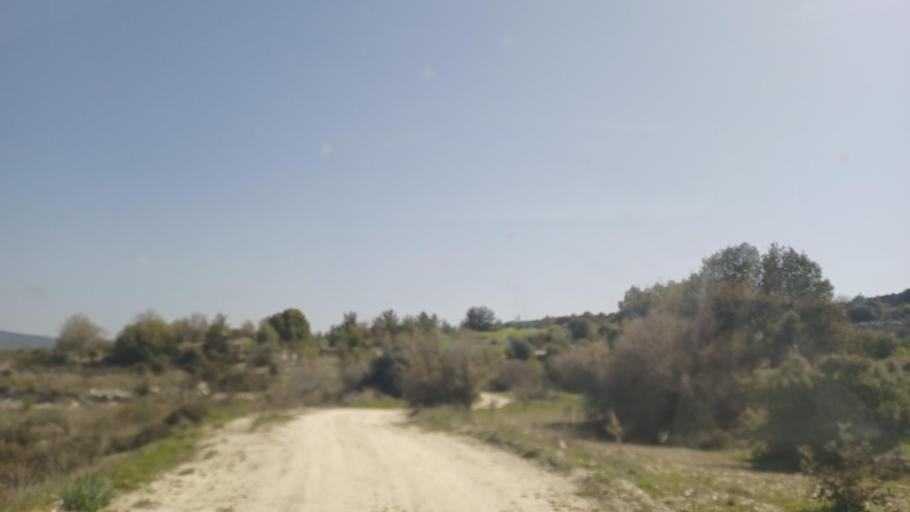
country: CY
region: Limassol
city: Pachna
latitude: 34.8740
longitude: 32.7000
